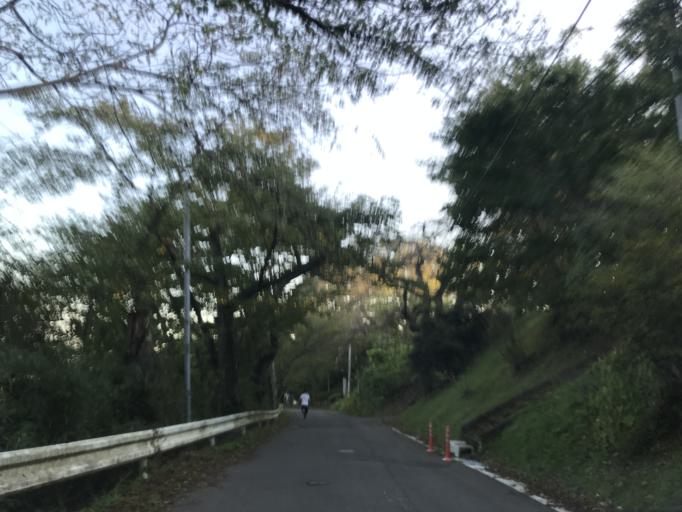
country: JP
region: Iwate
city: Mizusawa
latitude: 39.0510
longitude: 141.1194
